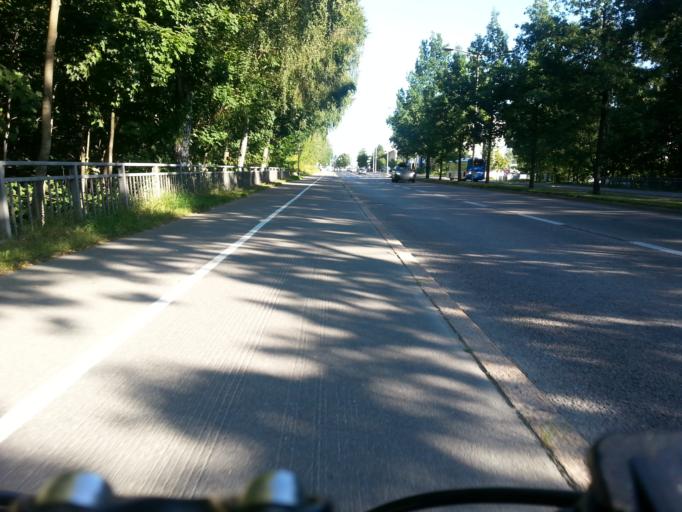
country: FI
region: Uusimaa
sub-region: Helsinki
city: Teekkarikylae
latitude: 60.2191
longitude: 24.8652
